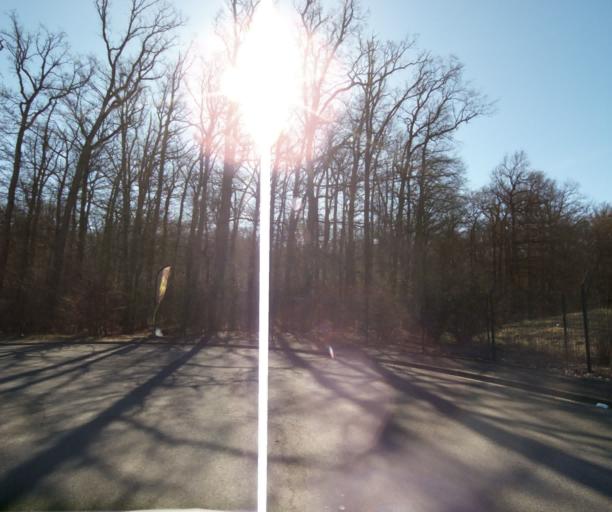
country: FR
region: Lorraine
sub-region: Departement de Meurthe-et-Moselle
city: Fleville-devant-Nancy
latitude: 48.6063
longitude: 6.1957
